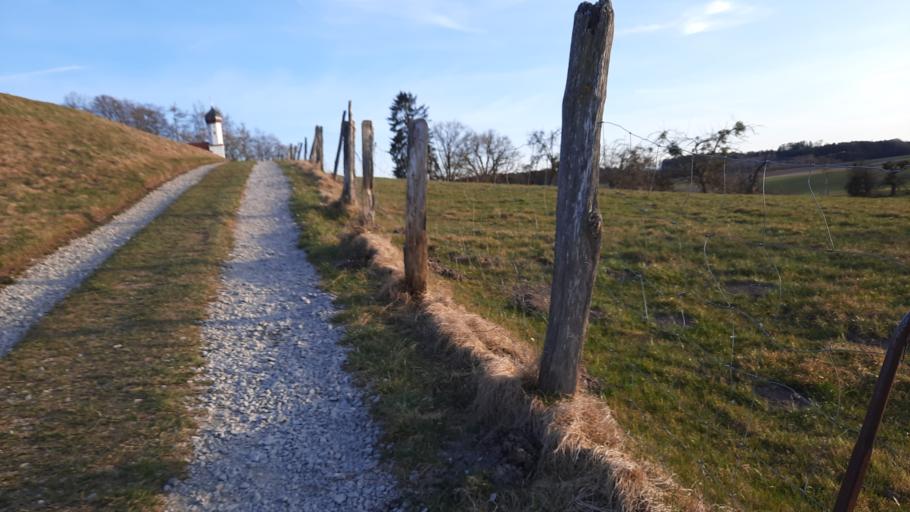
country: DE
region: Bavaria
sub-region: Upper Bavaria
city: Ebersberg
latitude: 48.0805
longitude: 11.9378
